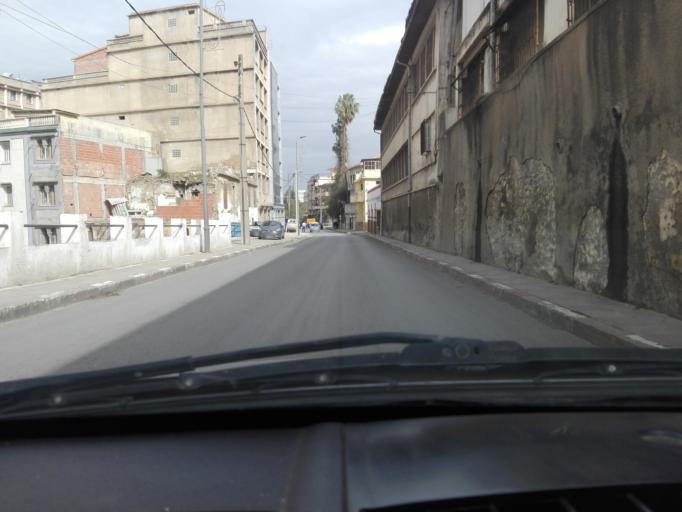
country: DZ
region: Alger
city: Bab Ezzouar
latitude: 36.7232
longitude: 3.1383
